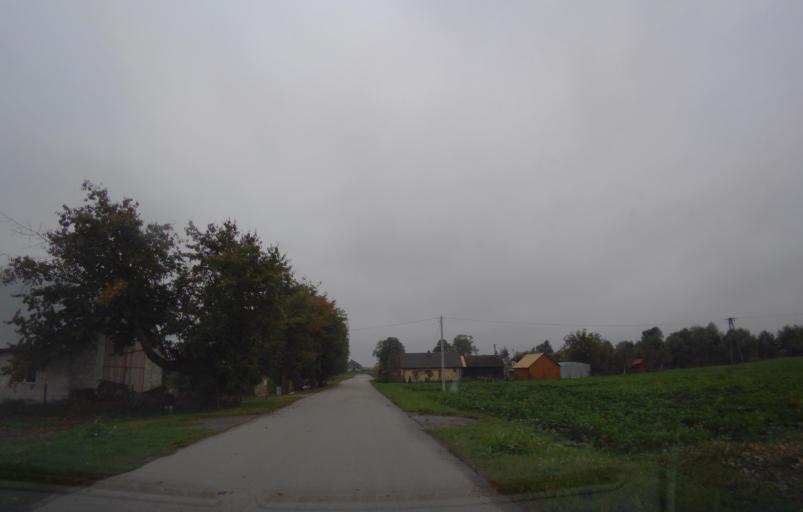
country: PL
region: Lublin Voivodeship
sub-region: Powiat chelmski
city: Sawin
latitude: 51.2131
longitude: 23.4593
